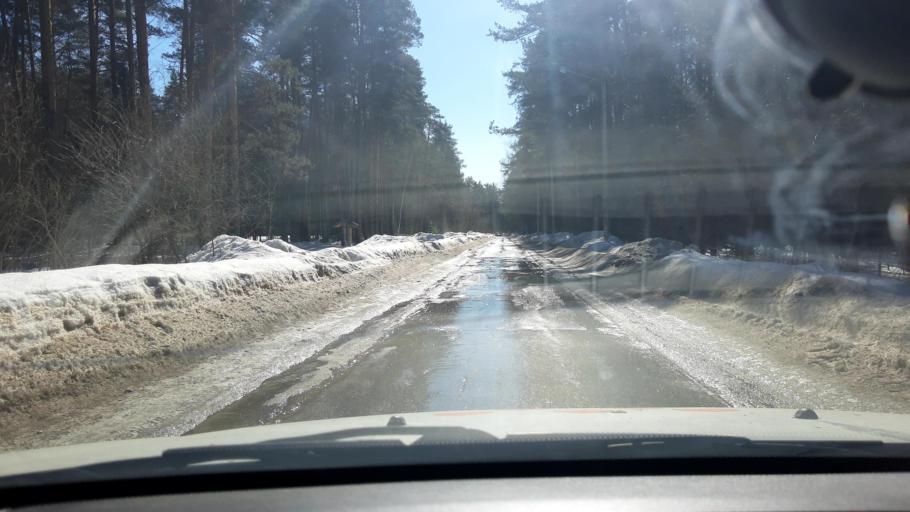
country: RU
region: Nizjnij Novgorod
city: Afonino
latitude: 56.1681
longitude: 44.0897
